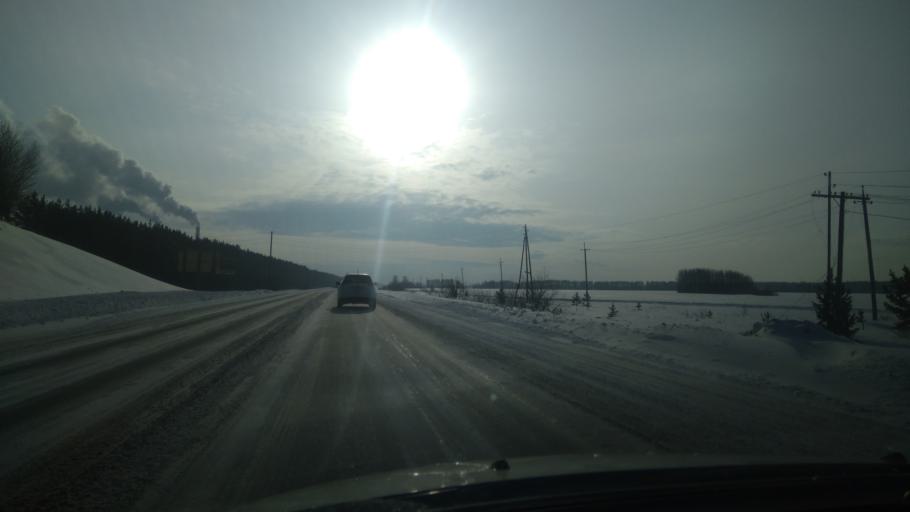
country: RU
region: Sverdlovsk
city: Sukhoy Log
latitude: 56.8788
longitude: 62.0450
